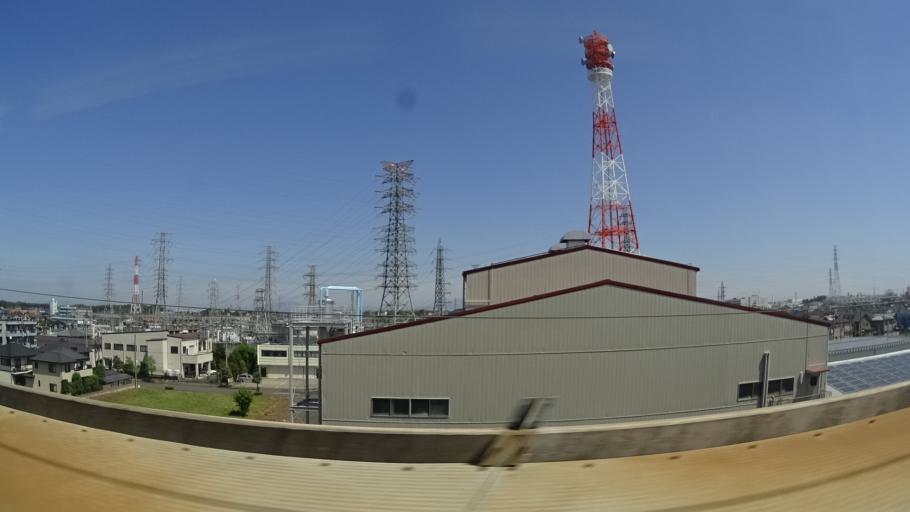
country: JP
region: Tochigi
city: Oyama
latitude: 36.3266
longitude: 139.8141
